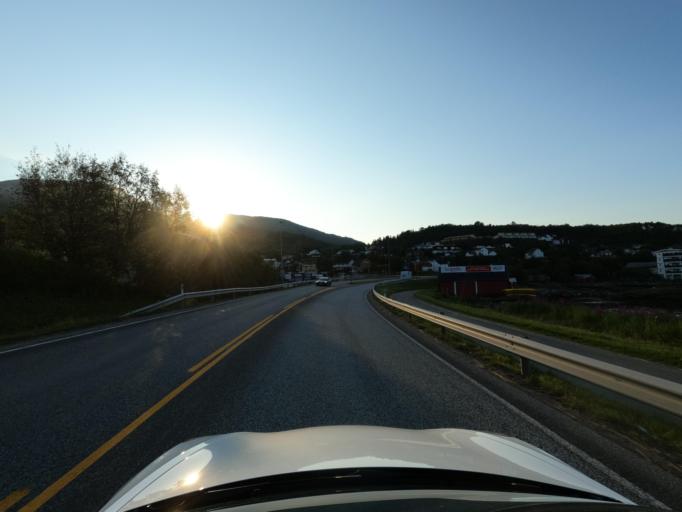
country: NO
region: Troms
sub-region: Harstad
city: Harstad
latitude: 68.7457
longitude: 16.5593
